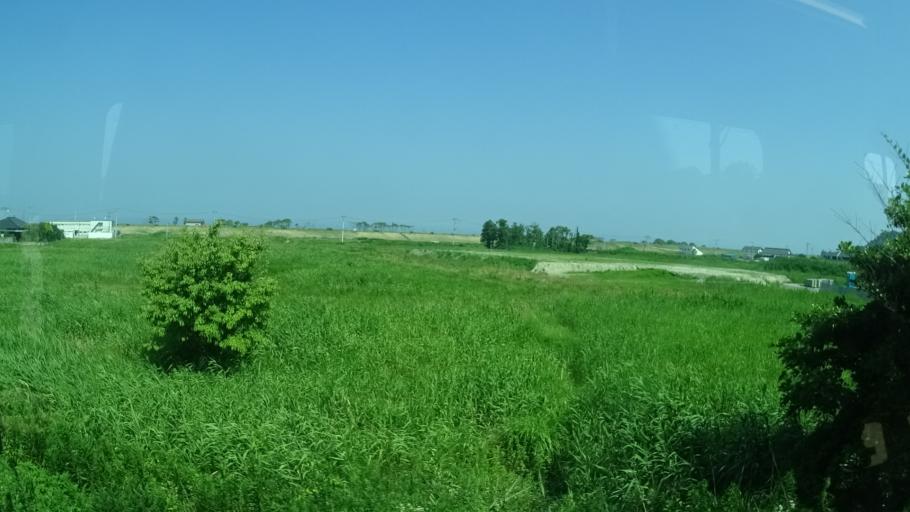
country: JP
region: Fukushima
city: Iwaki
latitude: 37.2147
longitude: 141.0014
